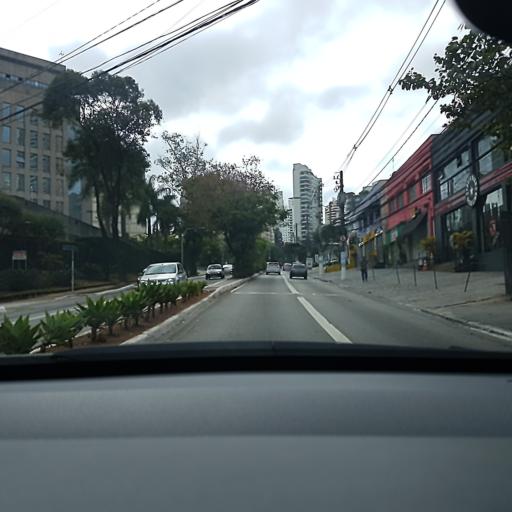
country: BR
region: Sao Paulo
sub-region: Taboao Da Serra
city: Taboao da Serra
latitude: -23.6295
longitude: -46.7362
